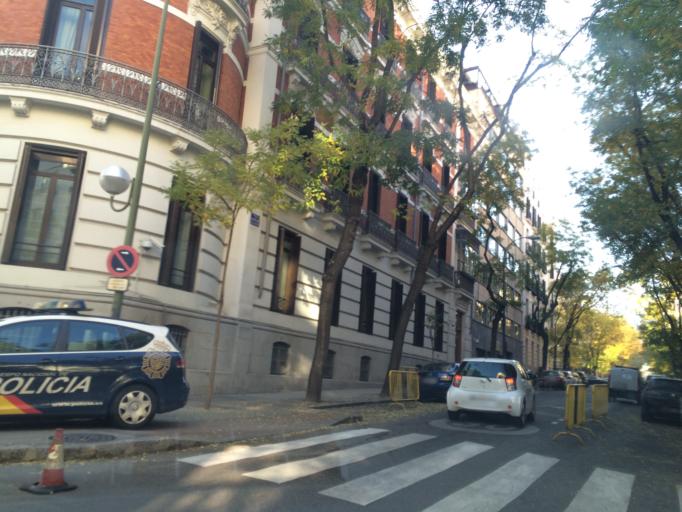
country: ES
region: Madrid
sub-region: Provincia de Madrid
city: Salamanca
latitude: 40.4282
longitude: -3.6911
